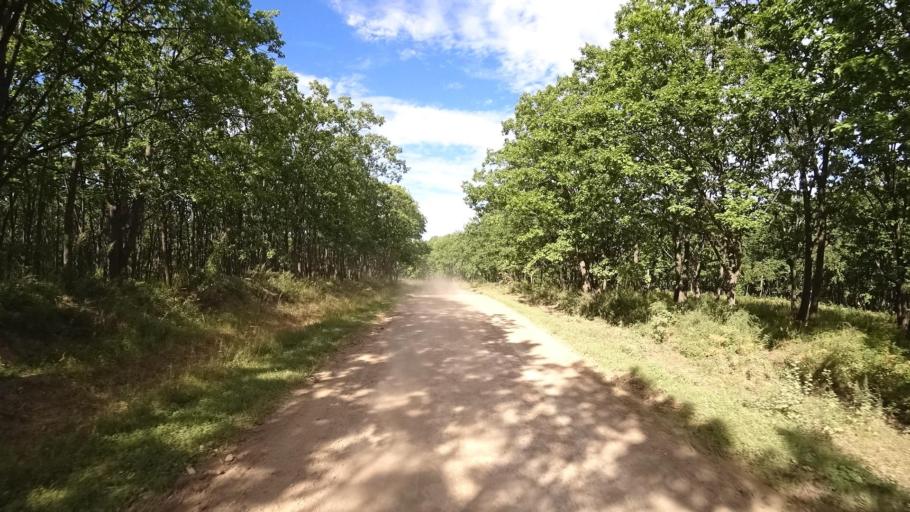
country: RU
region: Primorskiy
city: Yakovlevka
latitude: 44.4085
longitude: 133.5692
